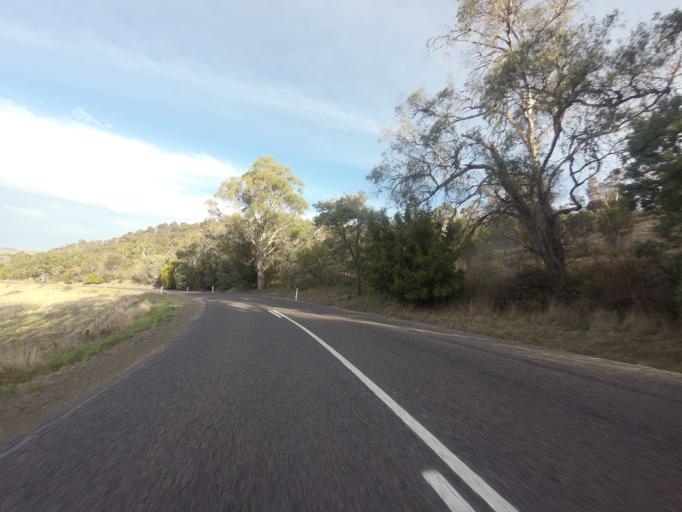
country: AU
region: Tasmania
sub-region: Brighton
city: Bridgewater
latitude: -42.4144
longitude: 147.1251
